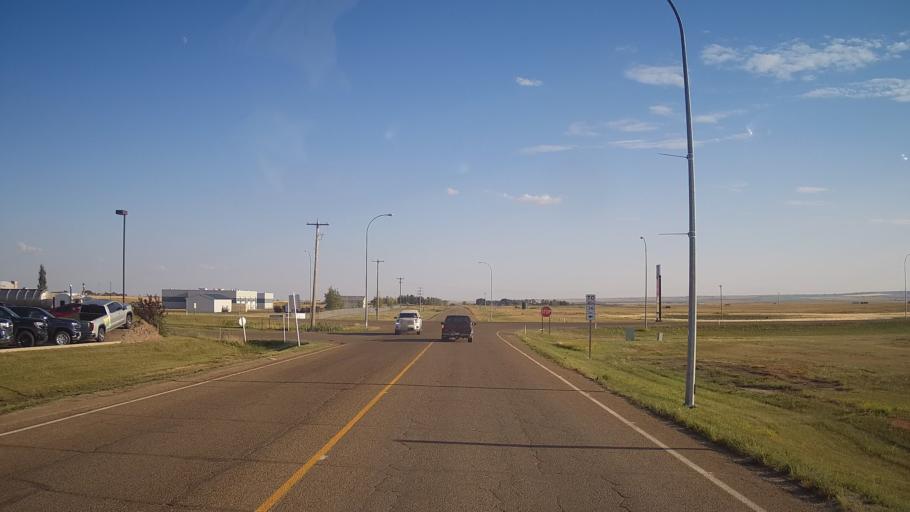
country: CA
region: Alberta
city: Hanna
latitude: 51.6353
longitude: -111.9420
